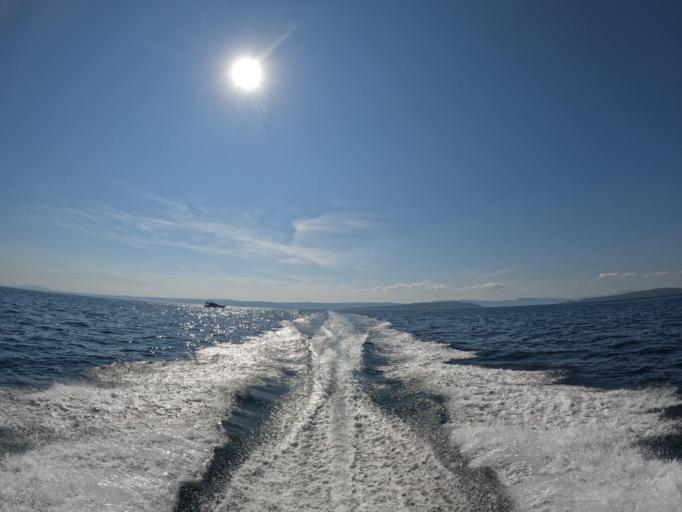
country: HR
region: Primorsko-Goranska
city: Punat
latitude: 44.9572
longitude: 14.6189
